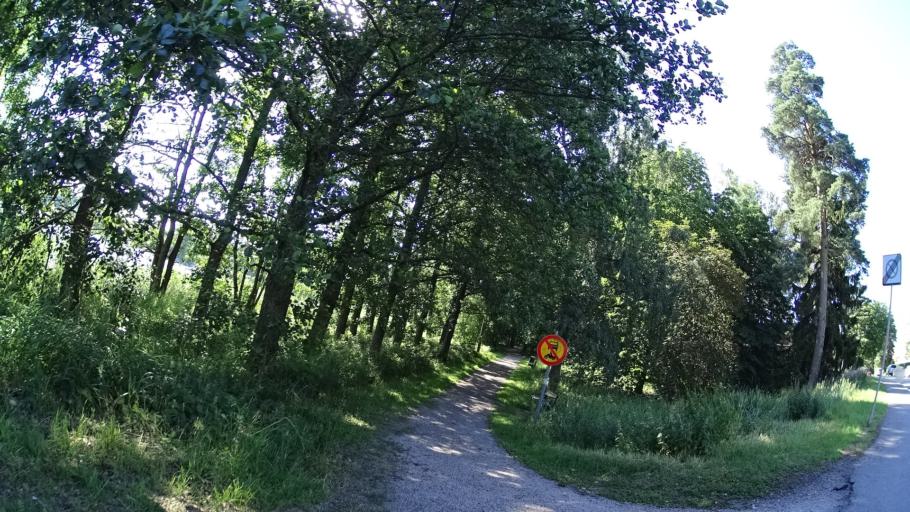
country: FI
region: Uusimaa
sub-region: Helsinki
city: Teekkarikylae
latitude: 60.1703
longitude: 24.8582
